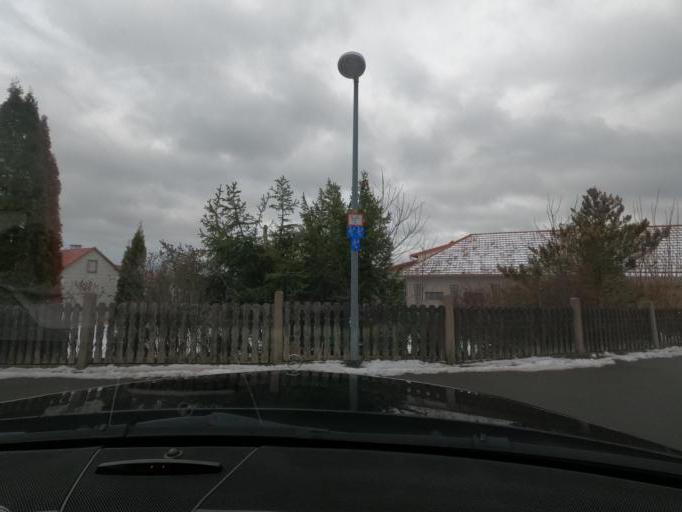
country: DE
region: Thuringia
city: Finsterbergen
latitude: 50.8333
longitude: 10.5925
